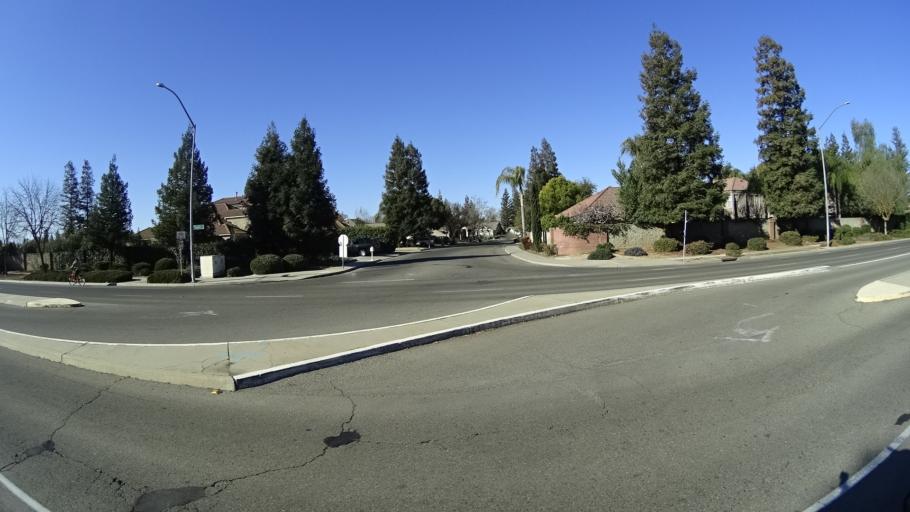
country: US
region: California
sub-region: Fresno County
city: Fresno
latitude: 36.8269
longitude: -119.8540
